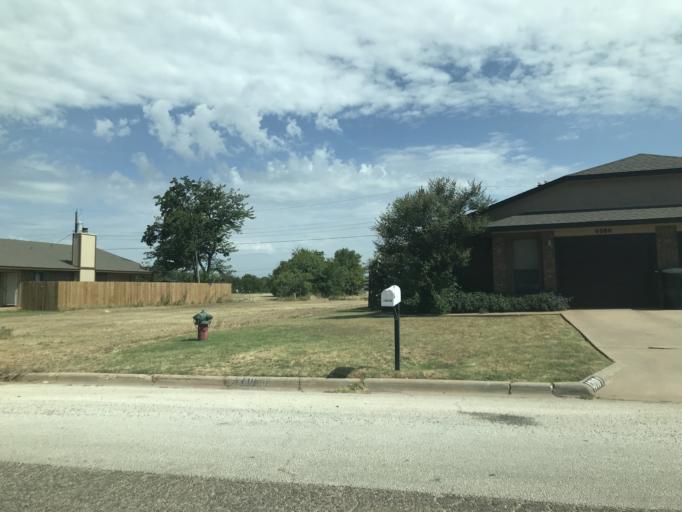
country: US
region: Texas
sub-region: Taylor County
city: Abilene
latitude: 32.4485
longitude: -99.7732
